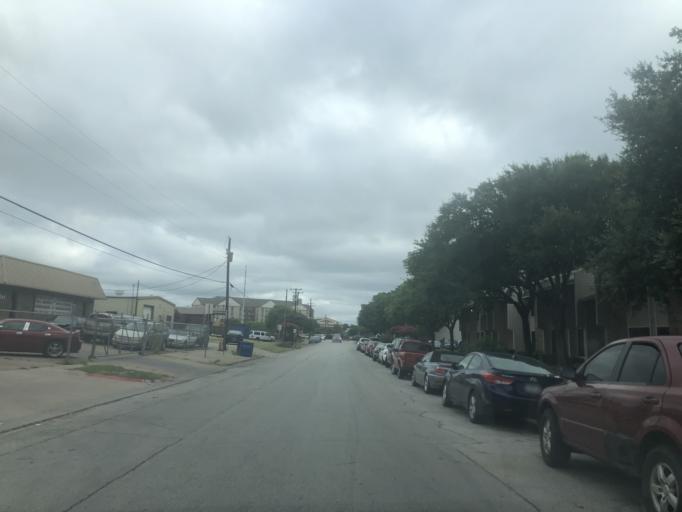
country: US
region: Texas
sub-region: Dallas County
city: Duncanville
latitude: 32.6601
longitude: -96.9058
